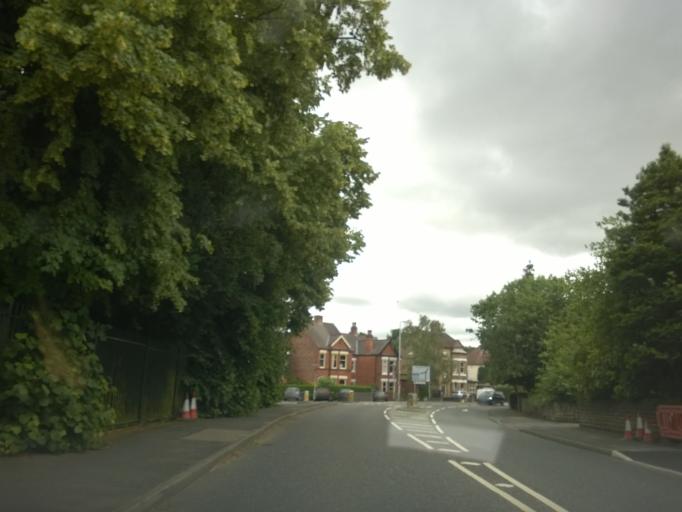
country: GB
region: England
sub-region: Leicestershire
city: Hinckley
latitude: 52.5452
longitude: -1.3632
